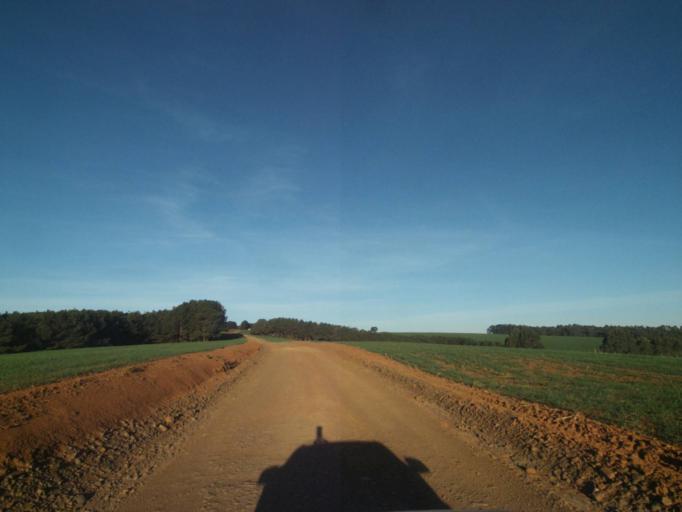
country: BR
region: Parana
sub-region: Telemaco Borba
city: Telemaco Borba
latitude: -24.4698
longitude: -50.5936
